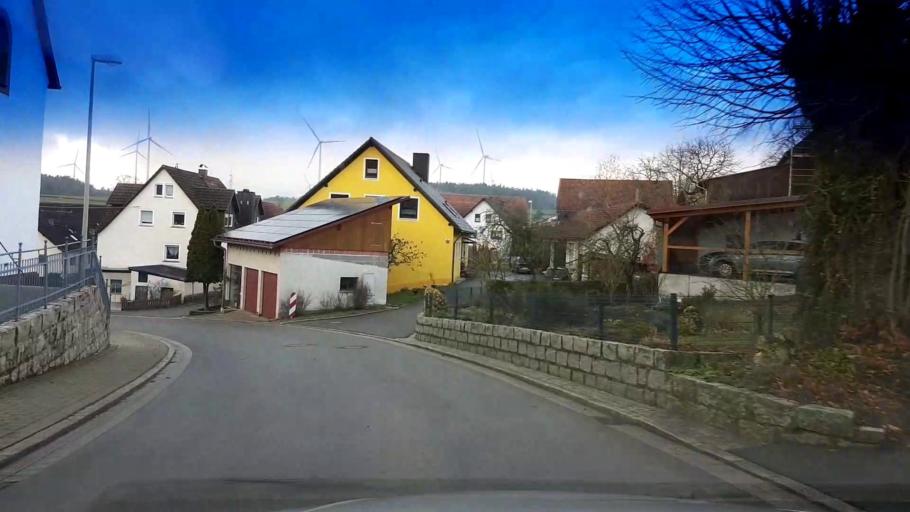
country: DE
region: Bavaria
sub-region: Upper Franconia
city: Poxdorf
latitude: 49.9365
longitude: 11.1236
